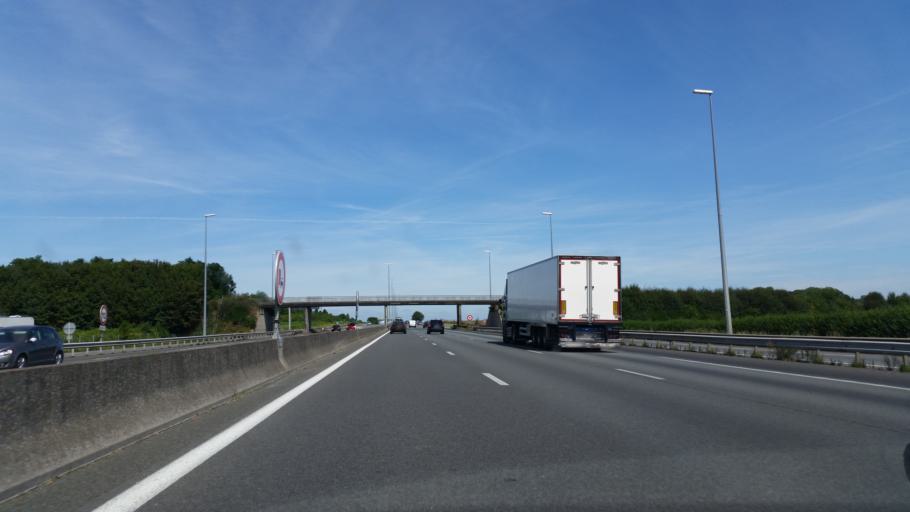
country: FR
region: Nord-Pas-de-Calais
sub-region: Departement du Pas-de-Calais
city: Fampoux
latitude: 50.2713
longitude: 2.8697
